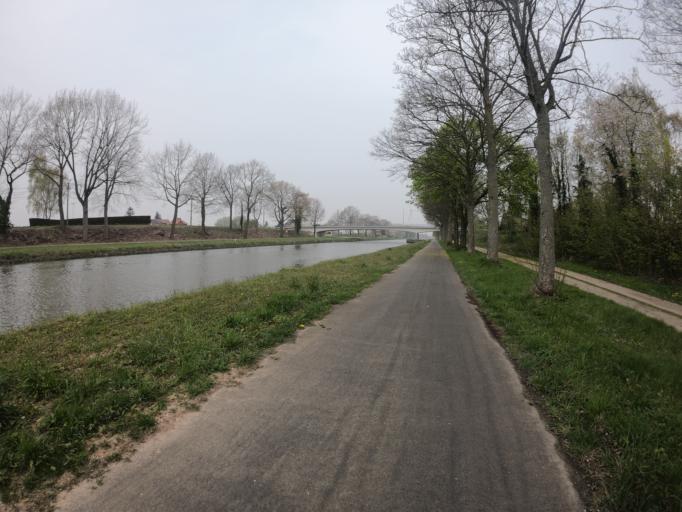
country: BE
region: Flanders
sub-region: Provincie Limburg
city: Maasmechelen
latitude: 50.9395
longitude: 5.7117
